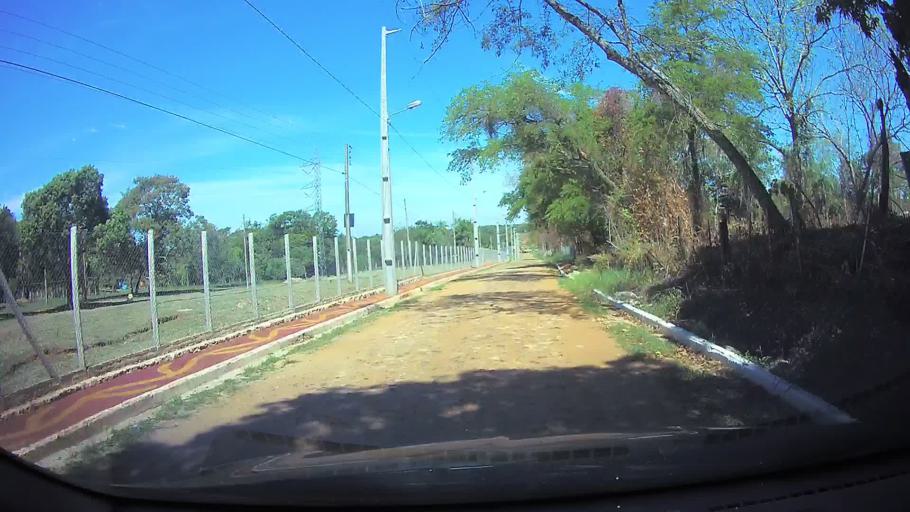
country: PY
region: Central
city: Limpio
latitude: -25.2336
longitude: -57.4380
